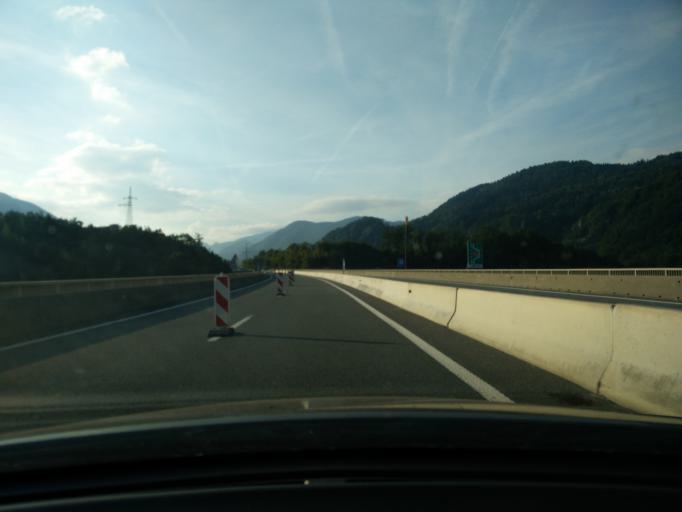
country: SI
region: Zirovnica
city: Zirovnica
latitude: 46.4077
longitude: 14.1264
